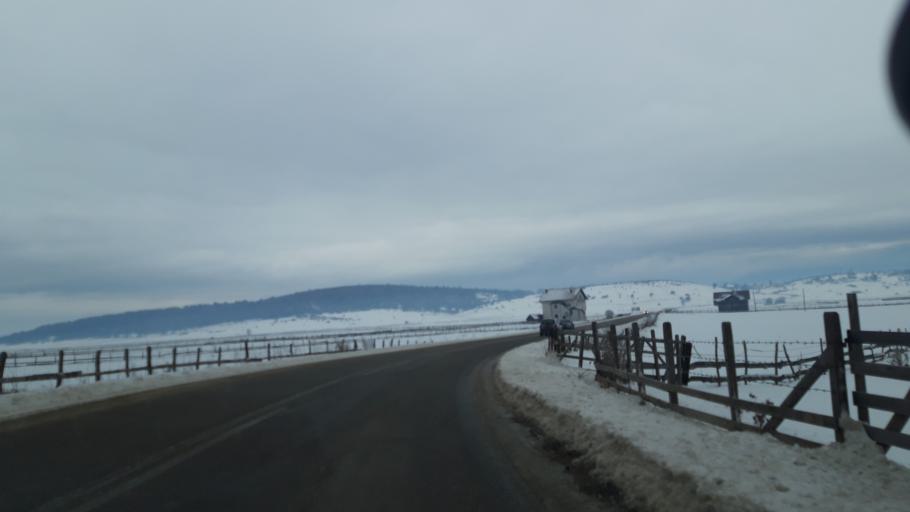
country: BA
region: Republika Srpska
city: Sokolac
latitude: 43.9613
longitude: 18.8563
